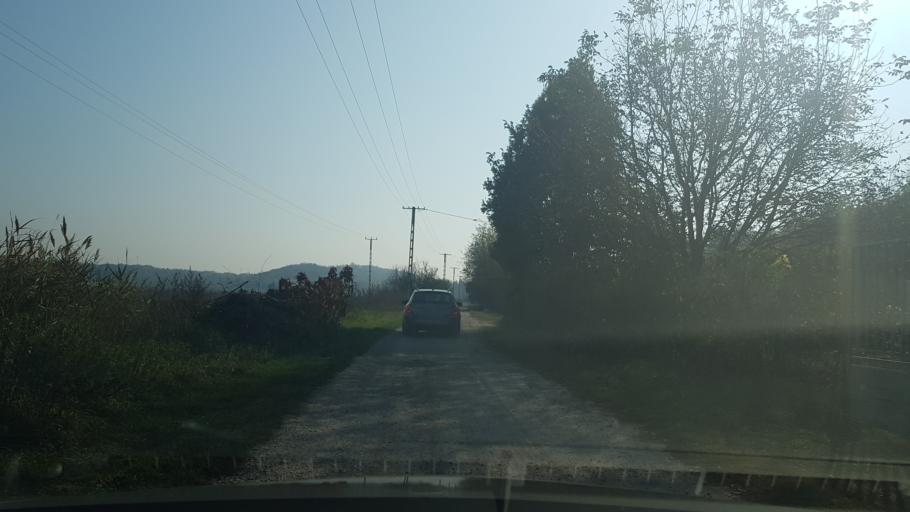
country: HU
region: Fejer
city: Adony
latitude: 47.0794
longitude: 18.8580
